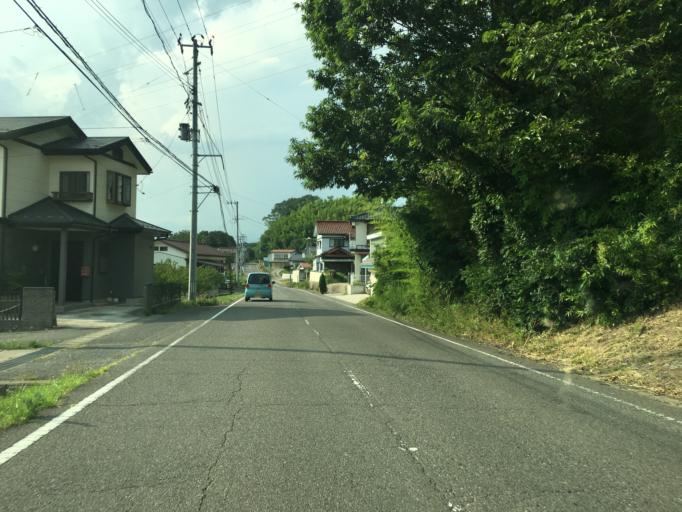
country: JP
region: Fukushima
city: Motomiya
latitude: 37.4573
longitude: 140.4254
